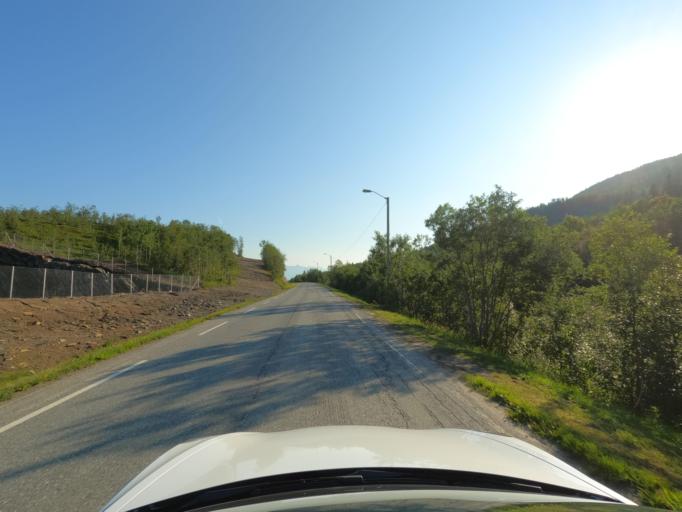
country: NO
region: Nordland
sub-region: Narvik
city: Bjerkvik
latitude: 68.5424
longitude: 17.4939
